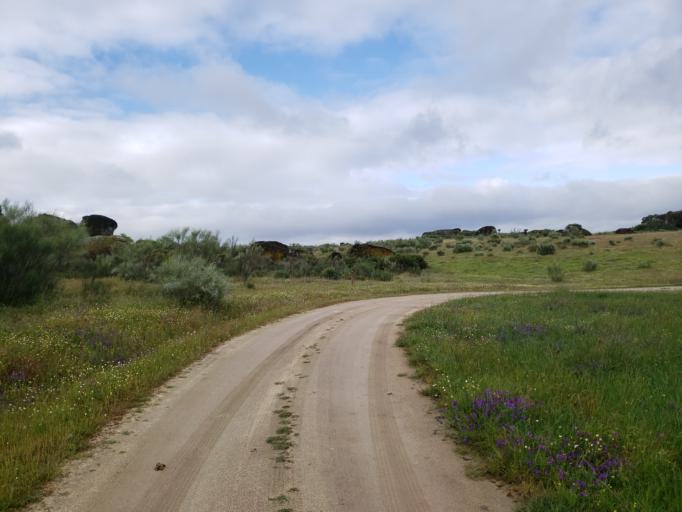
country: ES
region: Extremadura
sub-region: Provincia de Caceres
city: Malpartida de Caceres
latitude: 39.4247
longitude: -6.4850
